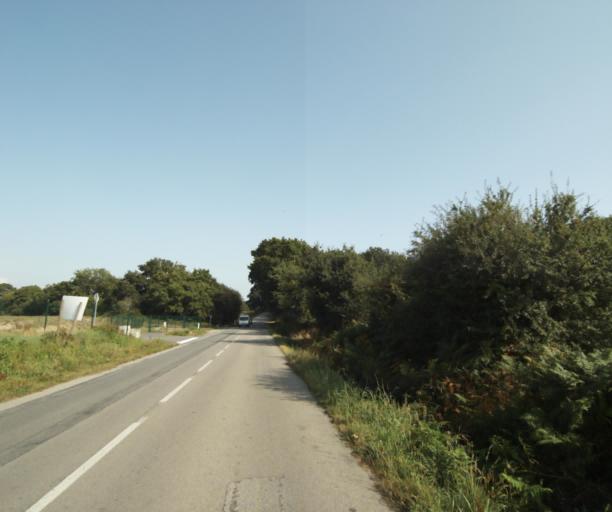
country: FR
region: Brittany
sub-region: Departement du Morbihan
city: Riantec
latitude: 47.7085
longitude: -3.2736
